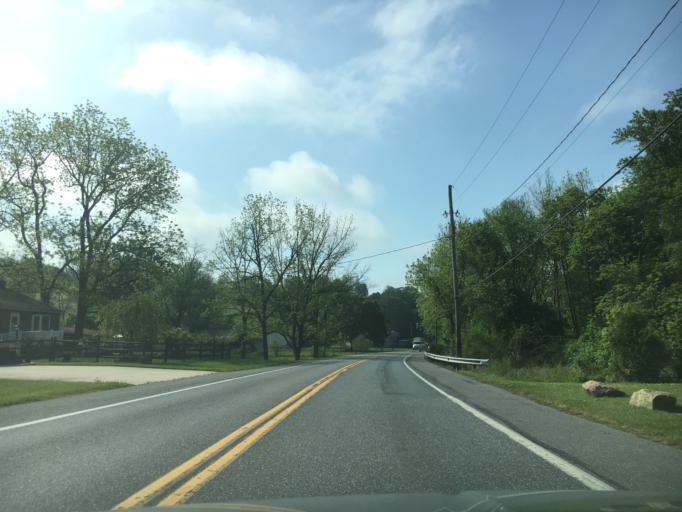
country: US
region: Pennsylvania
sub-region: Berks County
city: New Berlinville
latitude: 40.3542
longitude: -75.6636
